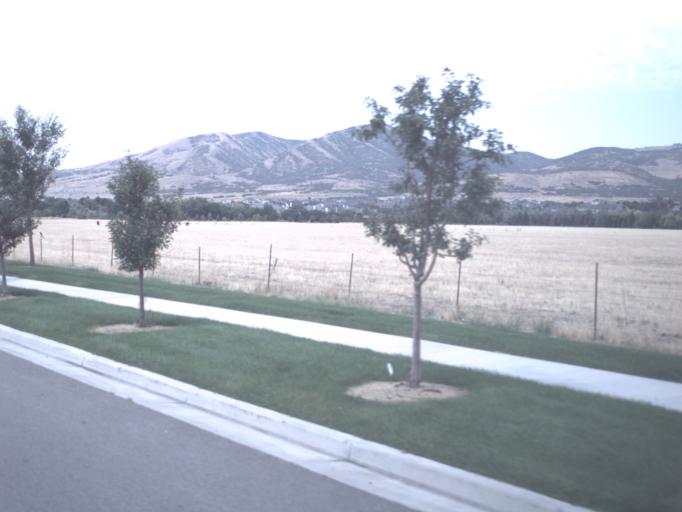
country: US
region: Utah
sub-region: Utah County
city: Alpine
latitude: 40.4319
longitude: -111.8044
